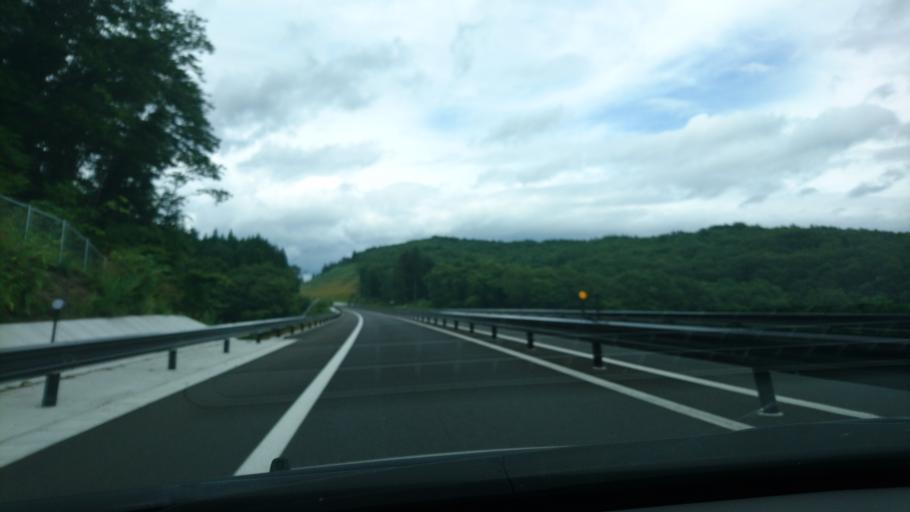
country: JP
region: Iwate
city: Yamada
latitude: 39.5455
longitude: 141.9241
